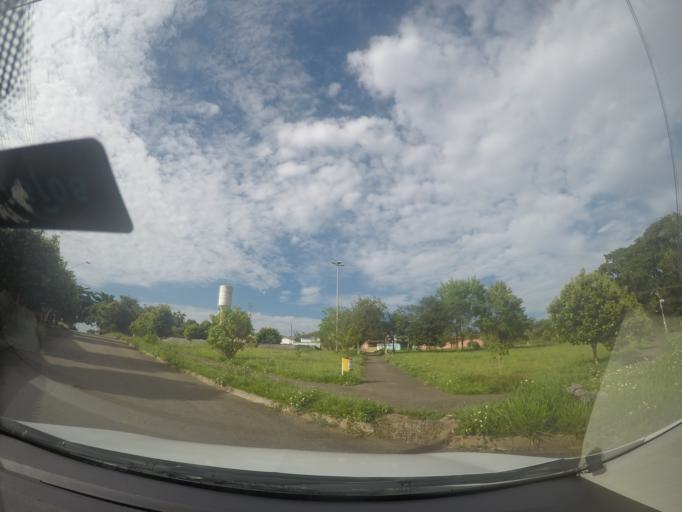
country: BR
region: Goias
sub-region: Goiania
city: Goiania
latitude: -16.6960
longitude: -49.1960
